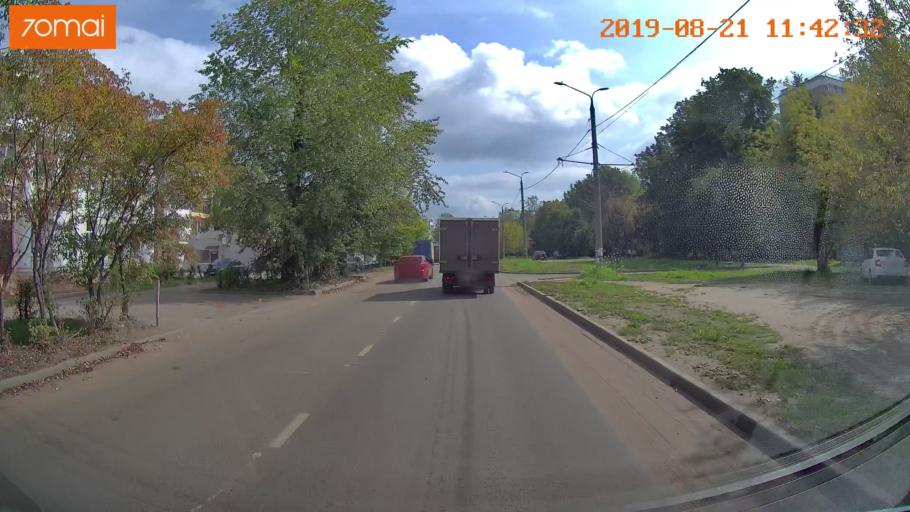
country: RU
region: Ivanovo
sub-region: Gorod Ivanovo
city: Ivanovo
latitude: 57.0020
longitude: 40.9504
